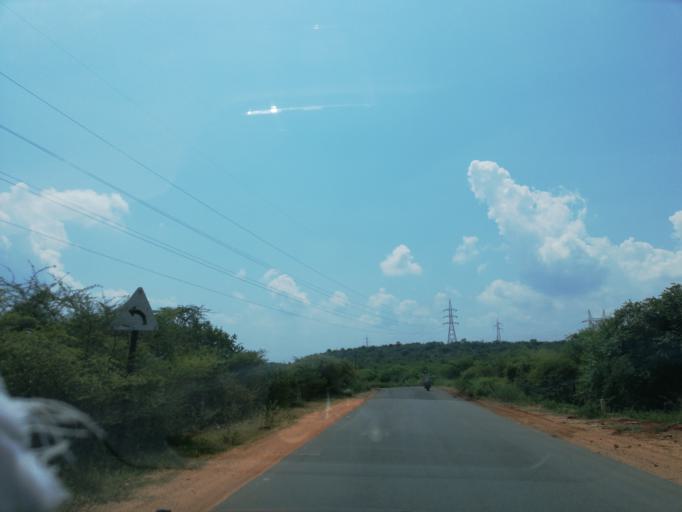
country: IN
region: Andhra Pradesh
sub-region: Guntur
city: Macherla
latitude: 16.5657
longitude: 79.3480
